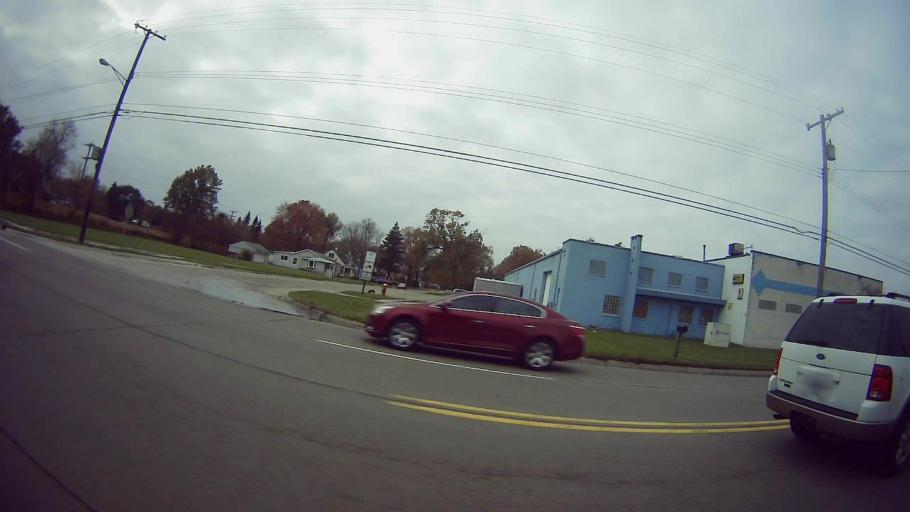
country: US
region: Michigan
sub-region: Oakland County
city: Hazel Park
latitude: 42.4527
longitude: -83.0641
